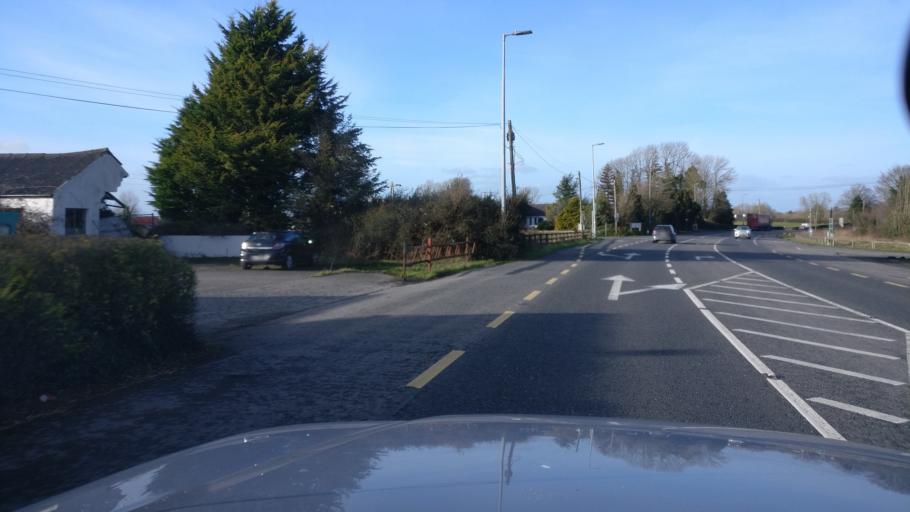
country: IE
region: Leinster
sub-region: Uibh Fhaili
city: Tullamore
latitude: 53.2208
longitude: -7.4749
